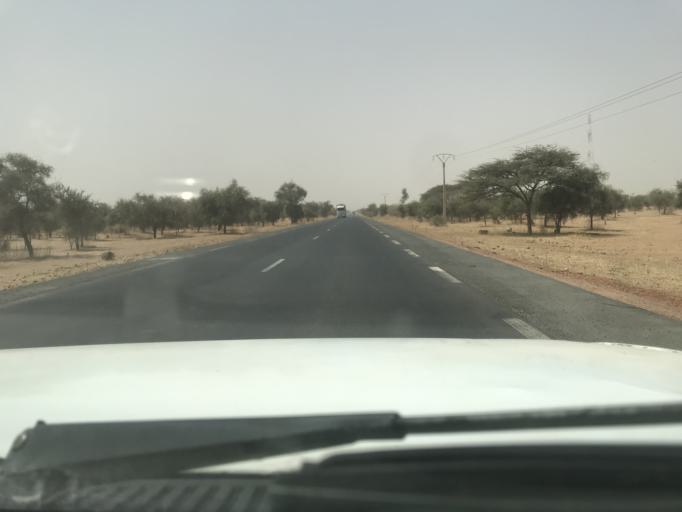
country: SN
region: Louga
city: Ndibene Dahra
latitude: 15.3477
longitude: -15.3336
